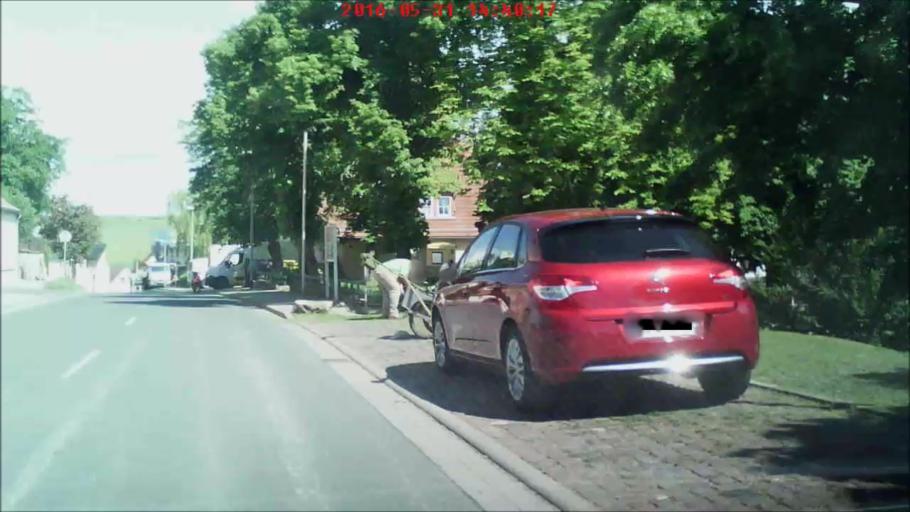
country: DE
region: Thuringia
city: Bilzingsleben
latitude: 51.2811
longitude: 11.0671
